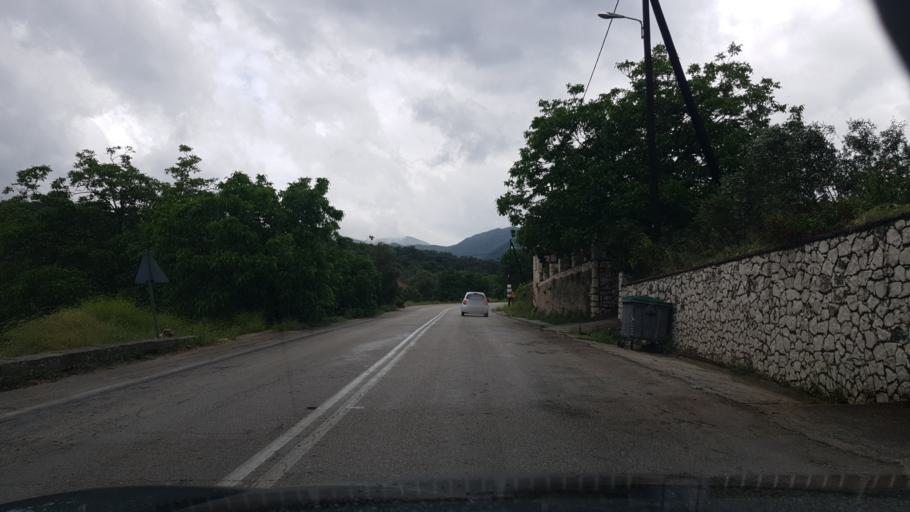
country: GR
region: Ionian Islands
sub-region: Lefkada
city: Nidri
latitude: 38.6304
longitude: 20.6495
